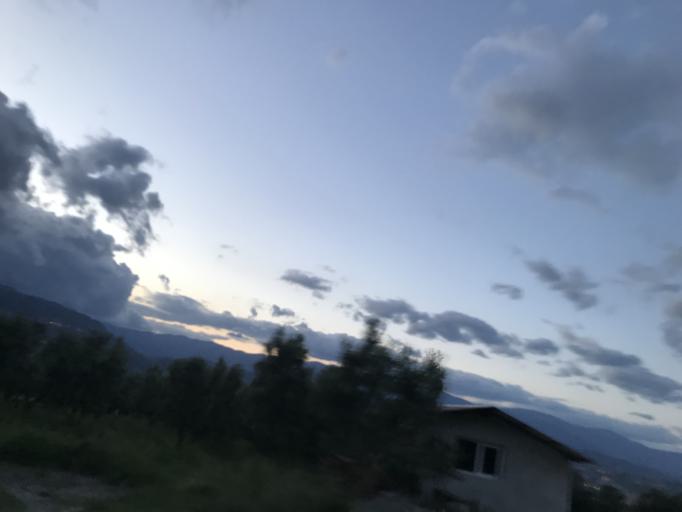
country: TR
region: Hatay
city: Uzunbag
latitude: 36.1200
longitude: 36.0456
